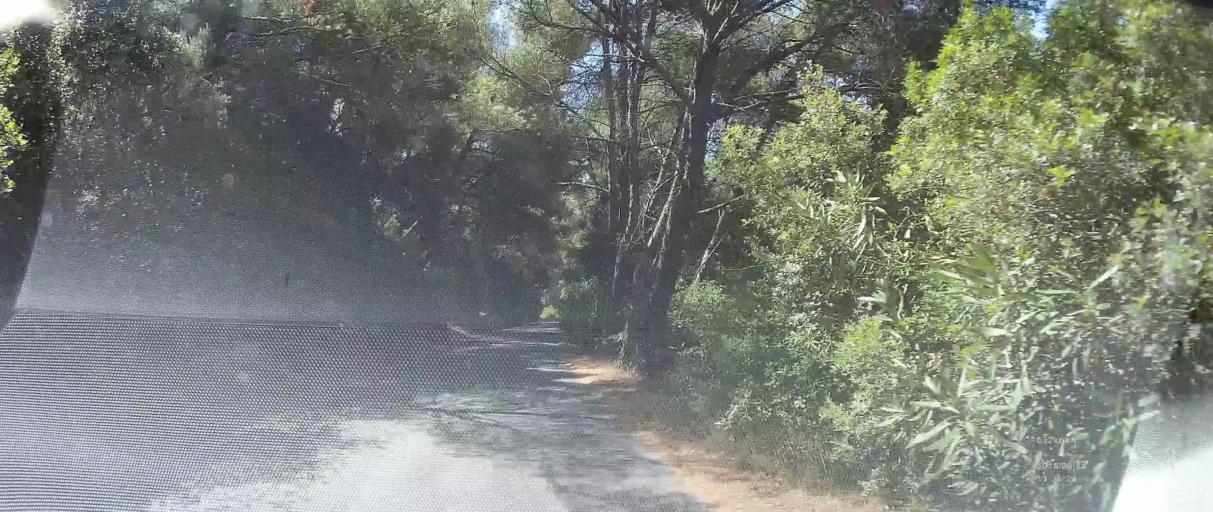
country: HR
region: Dubrovacko-Neretvanska
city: Blato
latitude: 42.7851
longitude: 17.3683
